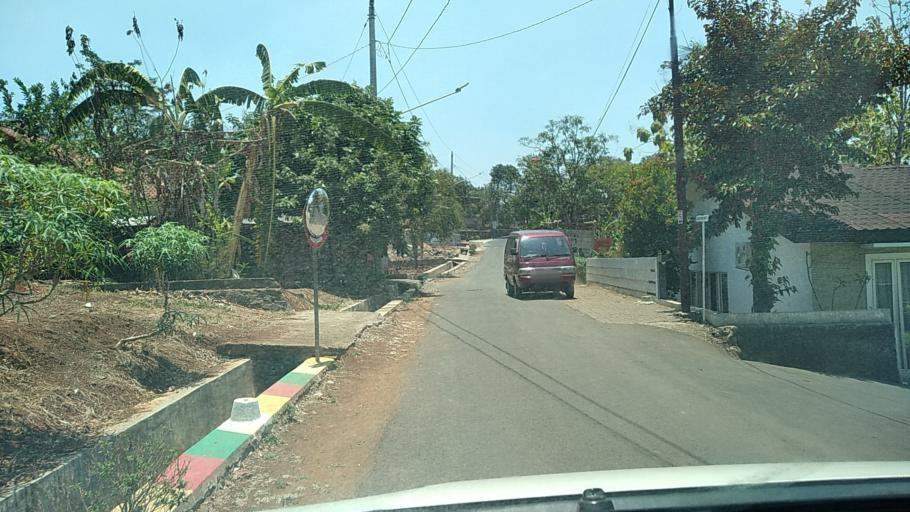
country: ID
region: Central Java
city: Semarang
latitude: -7.0576
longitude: 110.3900
